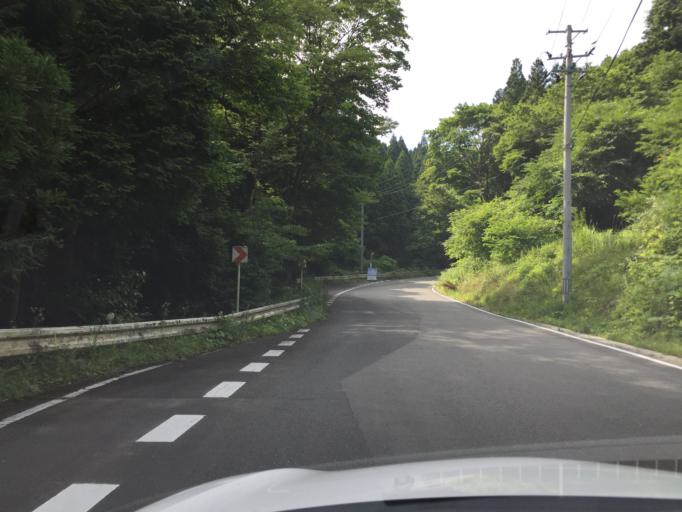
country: JP
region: Fukushima
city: Iwaki
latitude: 37.0774
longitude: 140.6862
